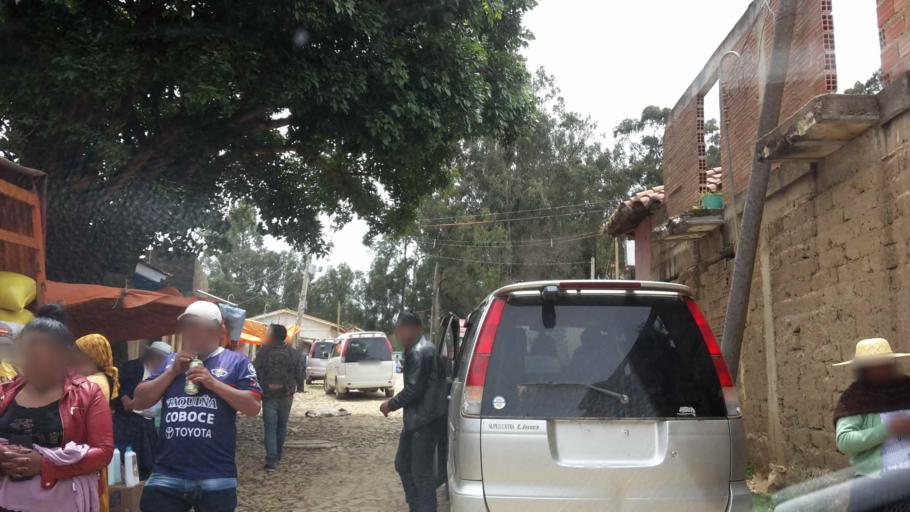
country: BO
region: Cochabamba
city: Totora
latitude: -17.7366
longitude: -65.1923
